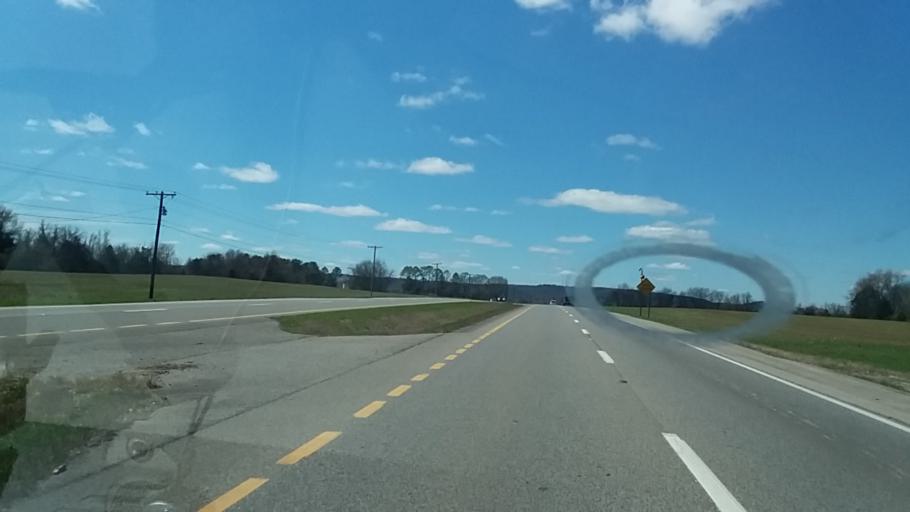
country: US
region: Alabama
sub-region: Colbert County
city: Tuscumbia
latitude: 34.7104
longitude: -87.7317
